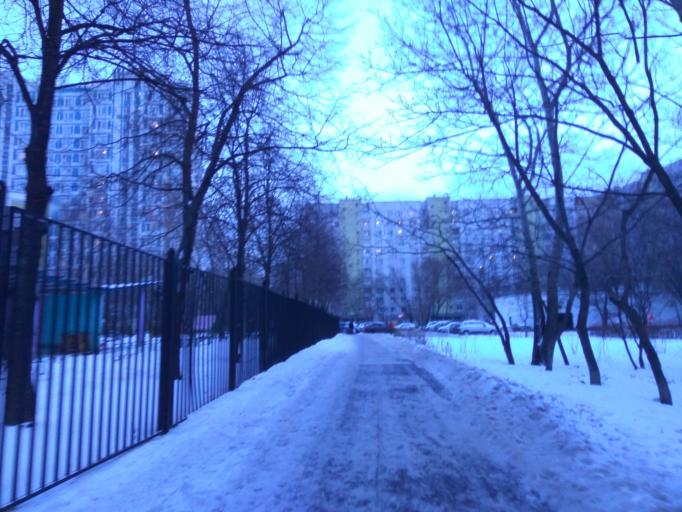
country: RU
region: Moscow
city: Mar'ino
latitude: 55.6491
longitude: 37.7104
